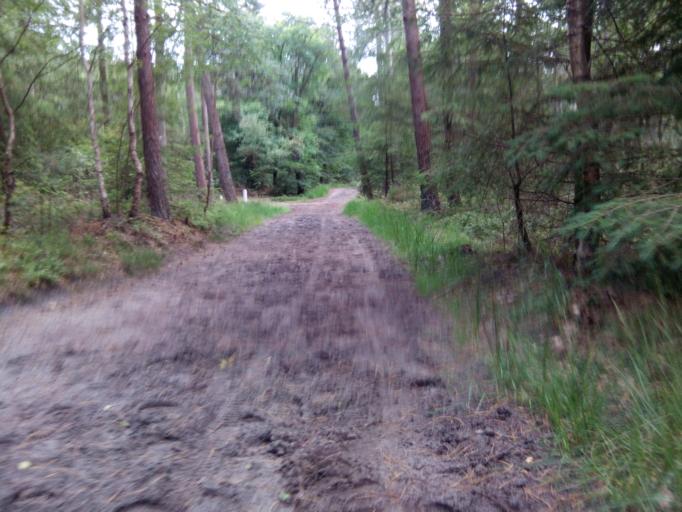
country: NL
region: Utrecht
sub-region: Gemeente Utrechtse Heuvelrug
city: Maarn
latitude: 52.0892
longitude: 5.3713
